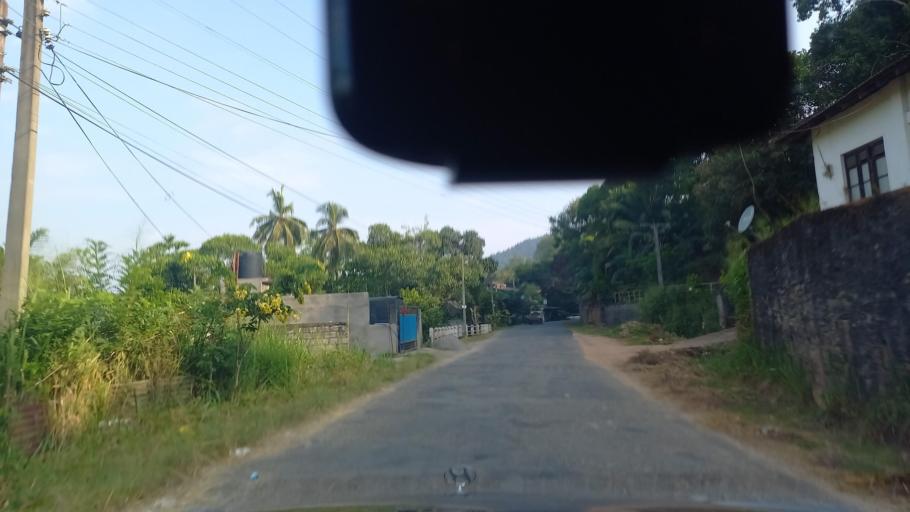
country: LK
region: Central
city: Gampola
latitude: 7.2275
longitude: 80.6036
